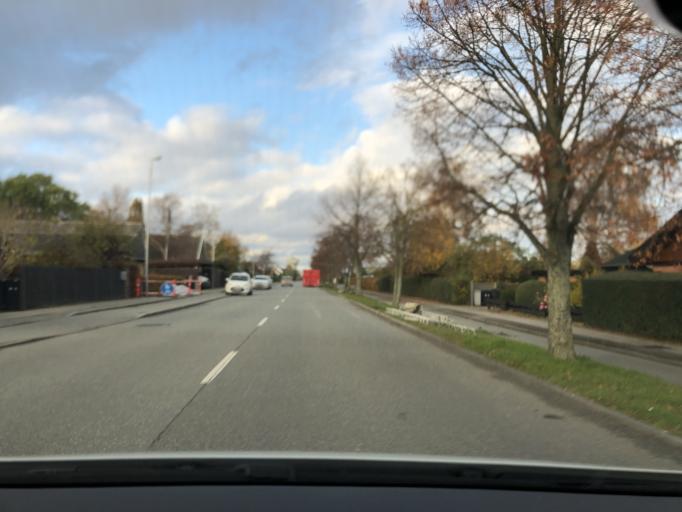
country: DK
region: Capital Region
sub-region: Tarnby Kommune
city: Tarnby
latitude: 55.6135
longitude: 12.5930
